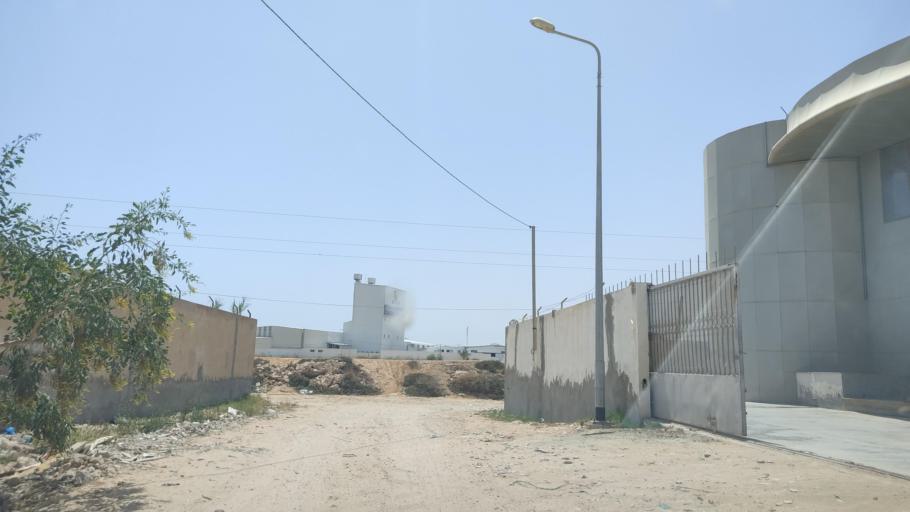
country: TN
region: Safaqis
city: Sfax
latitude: 34.7090
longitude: 10.7269
